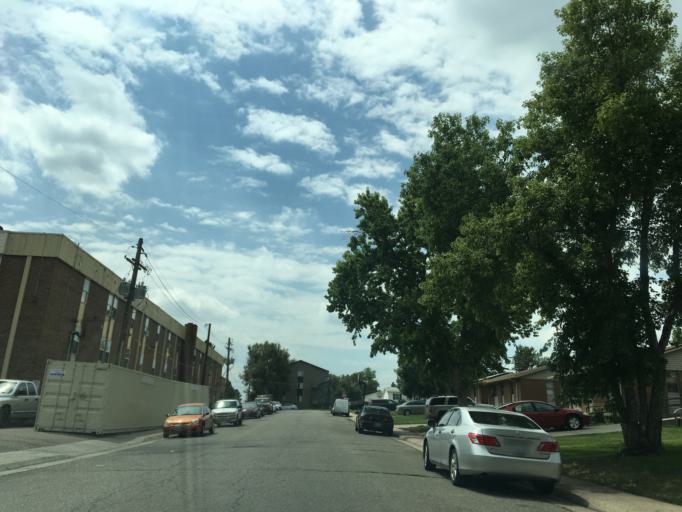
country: US
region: Colorado
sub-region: Arapahoe County
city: Sheridan
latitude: 39.6663
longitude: -105.0261
